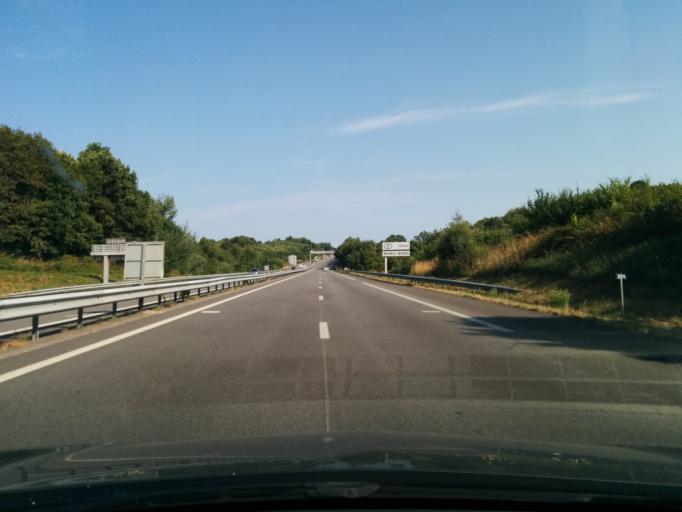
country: FR
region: Limousin
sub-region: Departement de la Haute-Vienne
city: Vicq-sur-Breuilh
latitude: 45.6327
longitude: 1.4306
